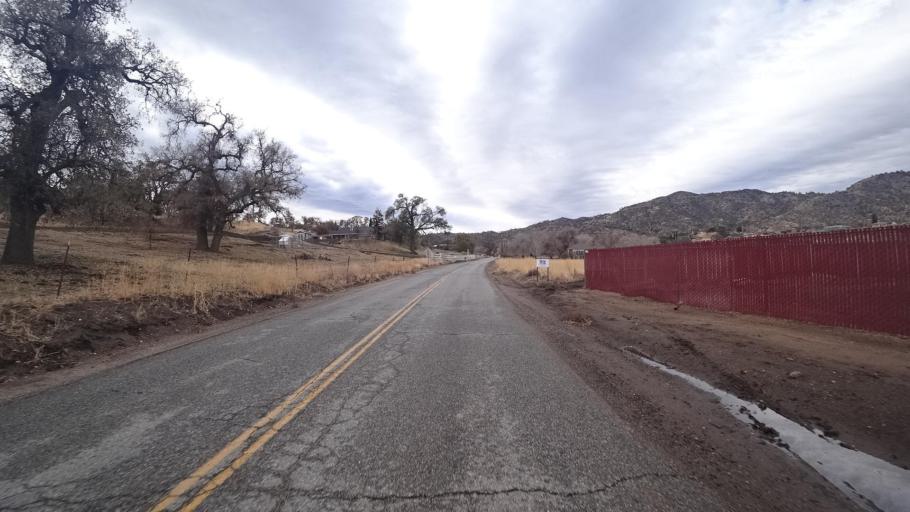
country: US
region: California
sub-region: Kern County
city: Golden Hills
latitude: 35.1415
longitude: -118.4965
